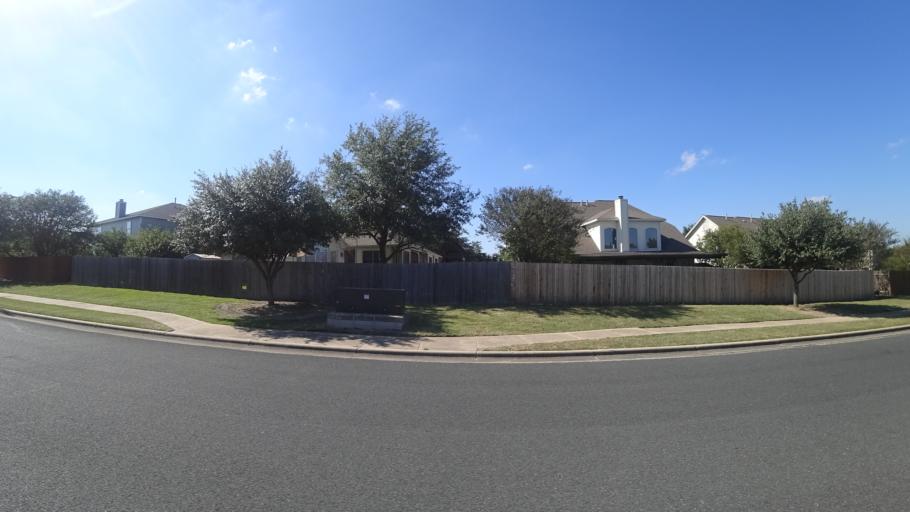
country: US
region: Texas
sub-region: Travis County
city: Manor
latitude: 30.3488
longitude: -97.6096
